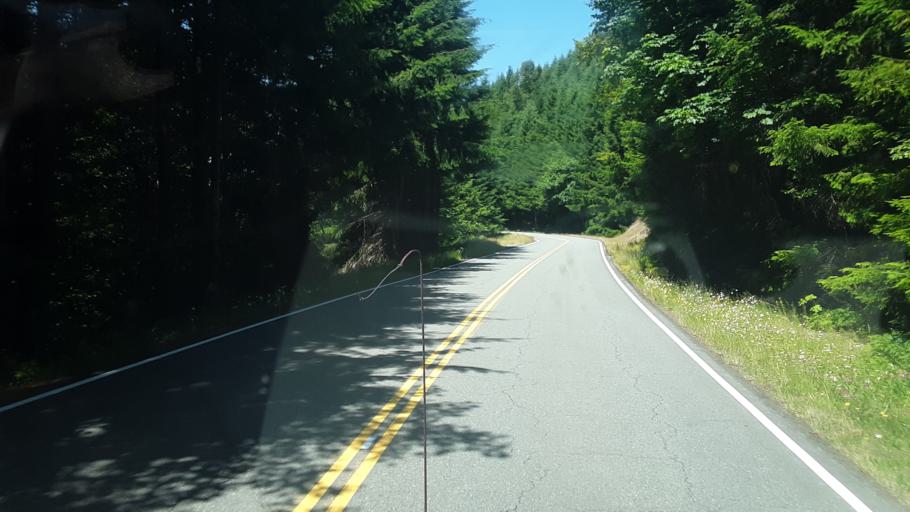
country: US
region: Washington
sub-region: Clark County
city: Yacolt
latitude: 46.0618
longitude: -122.1071
